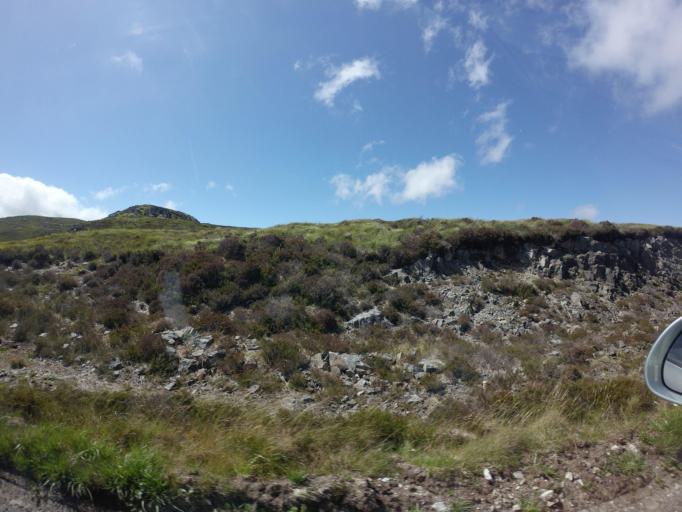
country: GB
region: Scotland
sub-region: Eilean Siar
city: Stornoway
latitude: 58.1416
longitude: -6.5074
